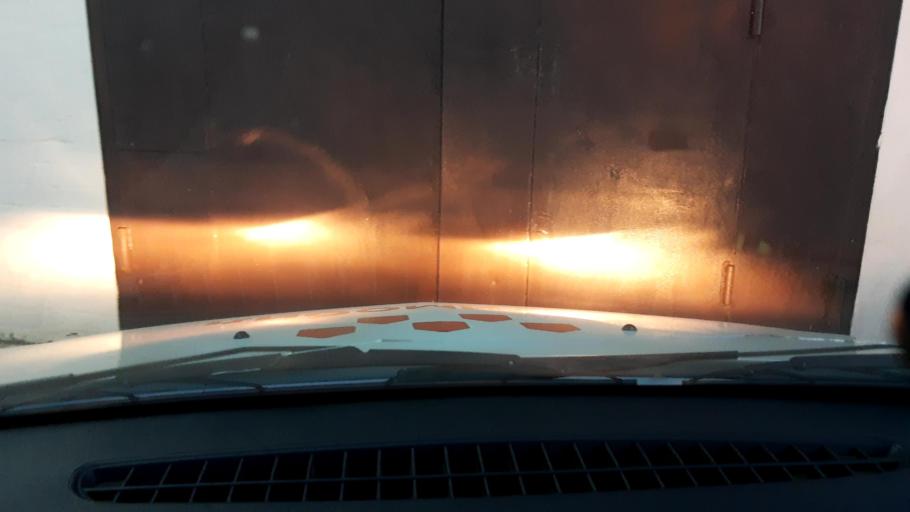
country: RU
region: Bashkortostan
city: Iglino
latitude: 54.7834
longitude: 56.2432
